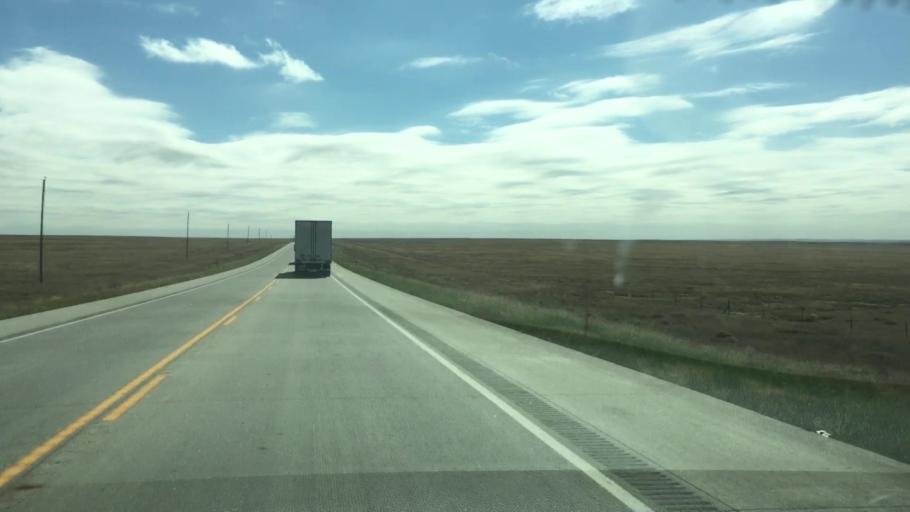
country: US
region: Colorado
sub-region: Lincoln County
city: Hugo
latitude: 39.0218
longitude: -103.3130
